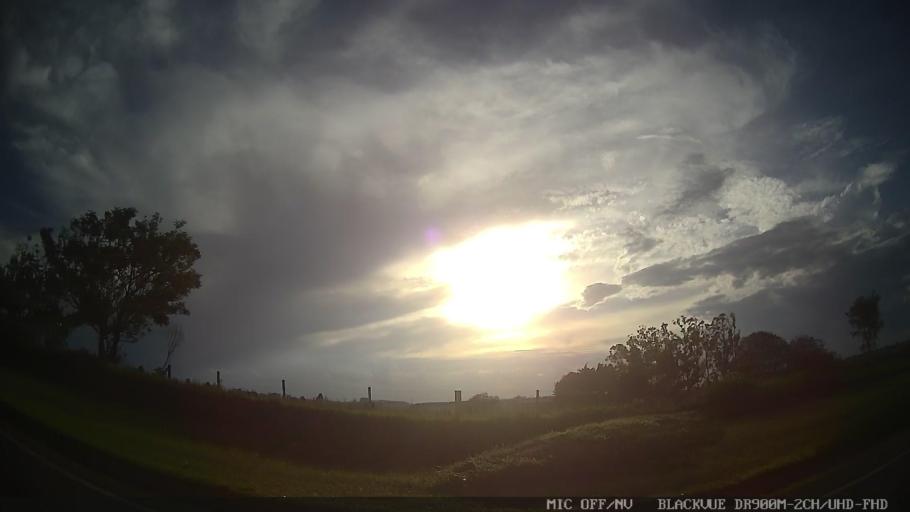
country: BR
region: Sao Paulo
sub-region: Tiete
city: Tiete
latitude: -23.1714
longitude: -47.6430
